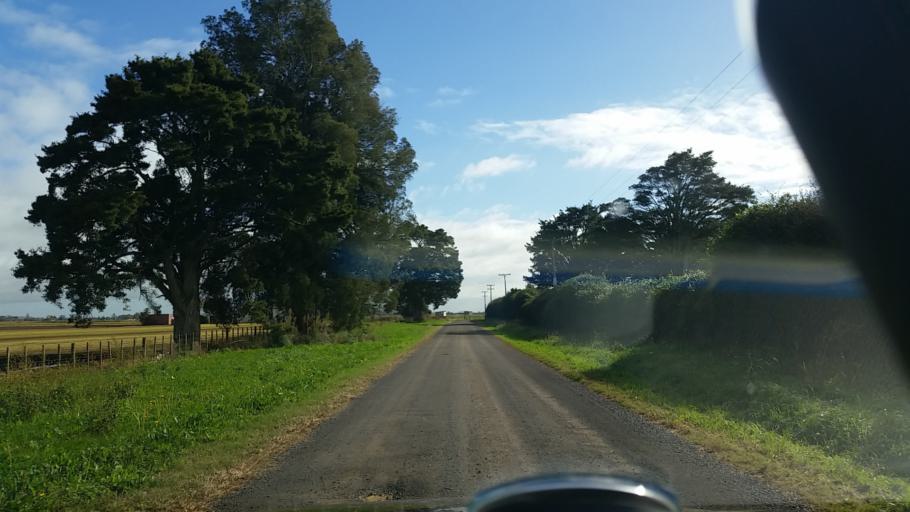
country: NZ
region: Waikato
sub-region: Matamata-Piako District
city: Matamata
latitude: -37.7396
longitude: 175.7559
